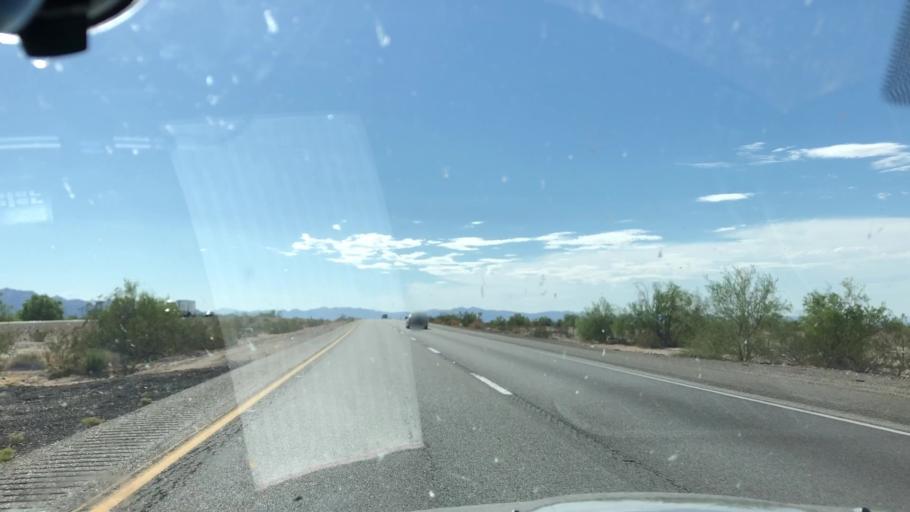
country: US
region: California
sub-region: Riverside County
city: Mesa Verde
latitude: 33.6614
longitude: -115.1716
